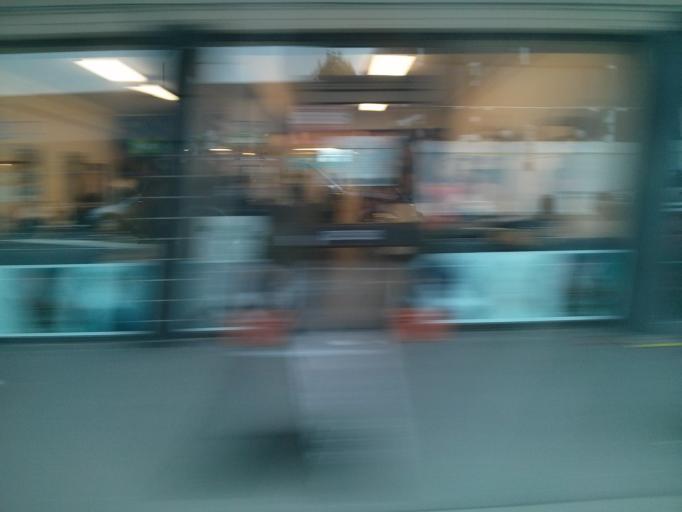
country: NZ
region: Canterbury
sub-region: Christchurch City
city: Christchurch
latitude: -43.4977
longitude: 172.6085
